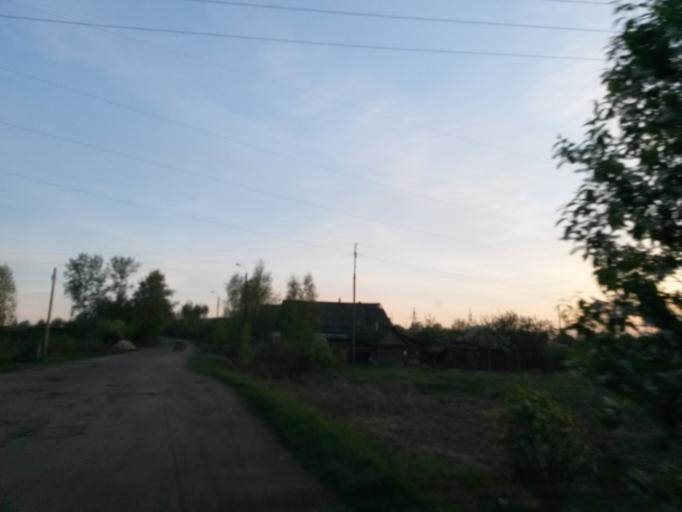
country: RU
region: Jaroslavl
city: Tutayev
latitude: 57.8924
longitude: 39.5604
